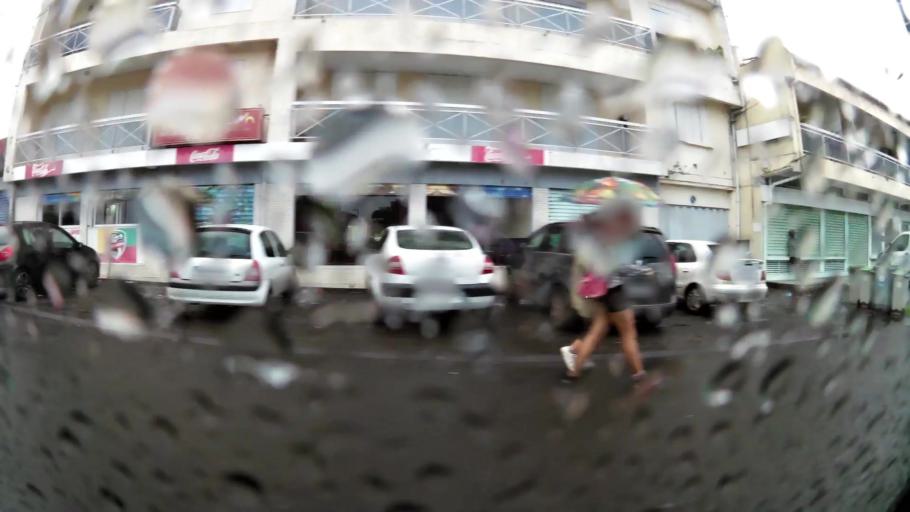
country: RE
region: Reunion
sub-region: Reunion
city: Saint-Benoit
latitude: -21.0362
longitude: 55.7152
